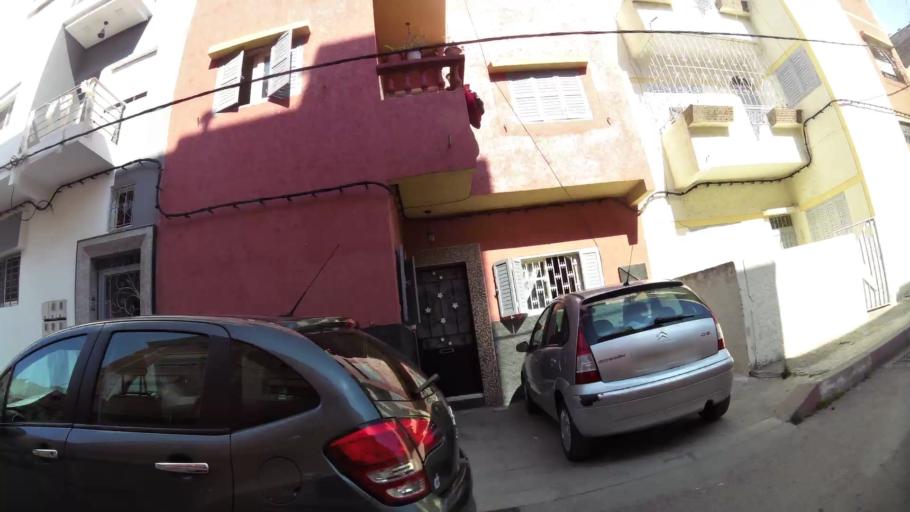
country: MA
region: Rabat-Sale-Zemmour-Zaer
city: Sale
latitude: 34.0463
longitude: -6.7780
